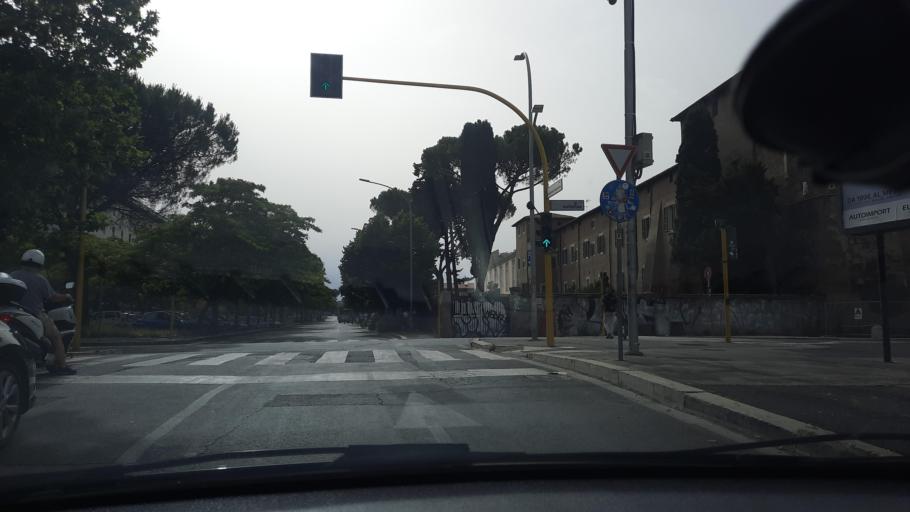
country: IT
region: Latium
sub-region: Citta metropolitana di Roma Capitale
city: Rome
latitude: 41.8569
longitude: 12.4777
